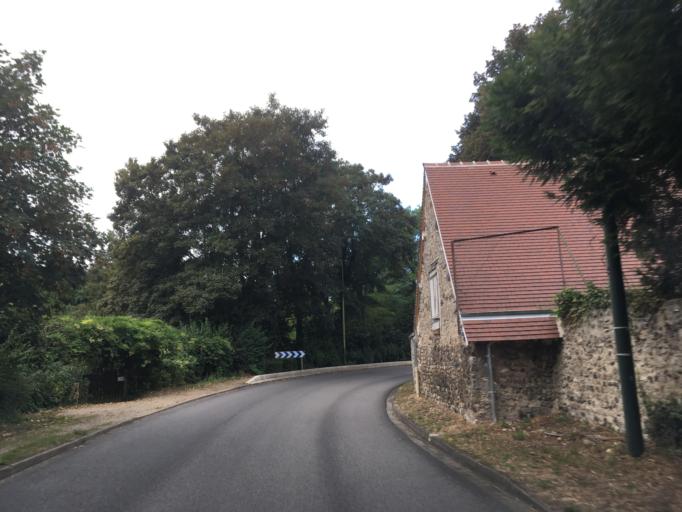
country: FR
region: Haute-Normandie
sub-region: Departement de l'Eure
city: Saint-Just
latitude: 49.1300
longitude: 1.4488
